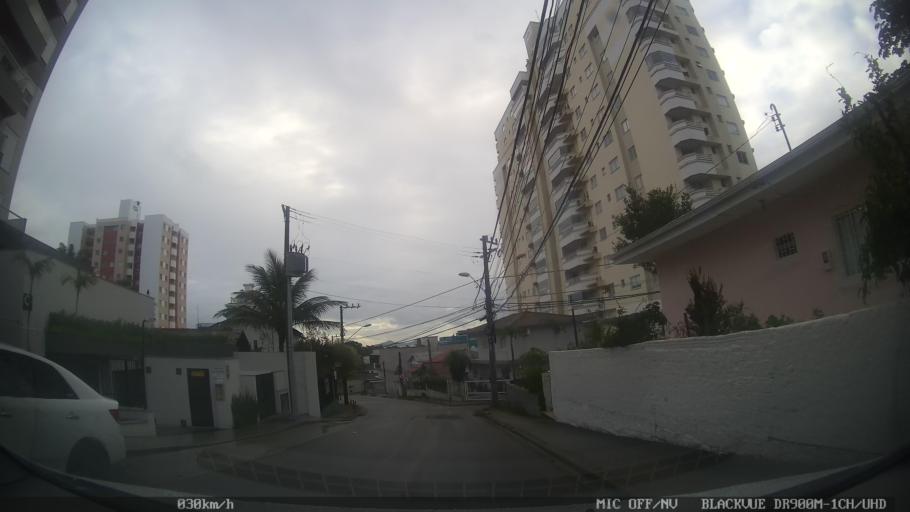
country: BR
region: Santa Catarina
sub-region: Sao Jose
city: Campinas
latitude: -27.5743
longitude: -48.6070
